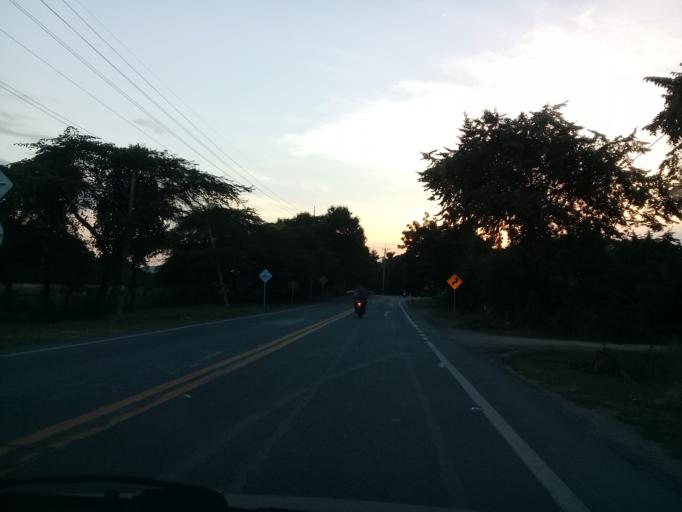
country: CO
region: Cundinamarca
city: Narino
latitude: 4.3649
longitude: -74.7864
